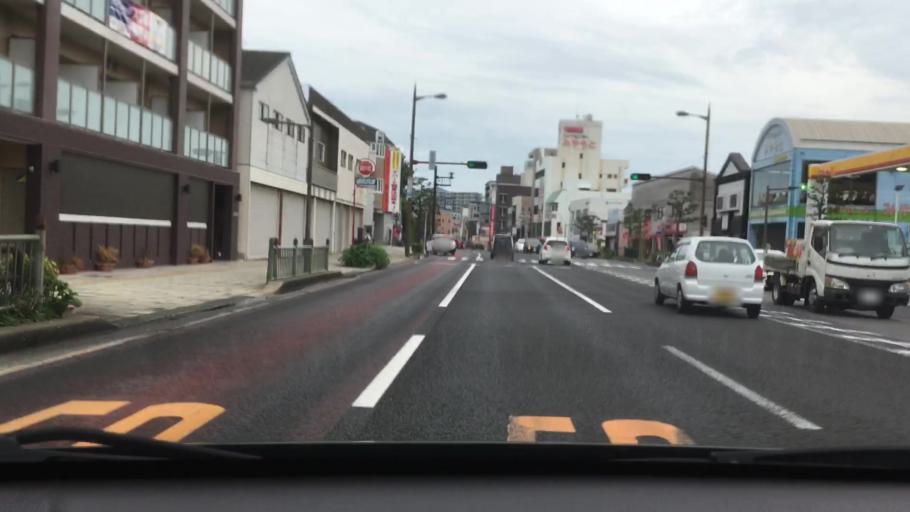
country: JP
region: Nagasaki
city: Nagasaki-shi
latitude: 32.7763
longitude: 129.8621
